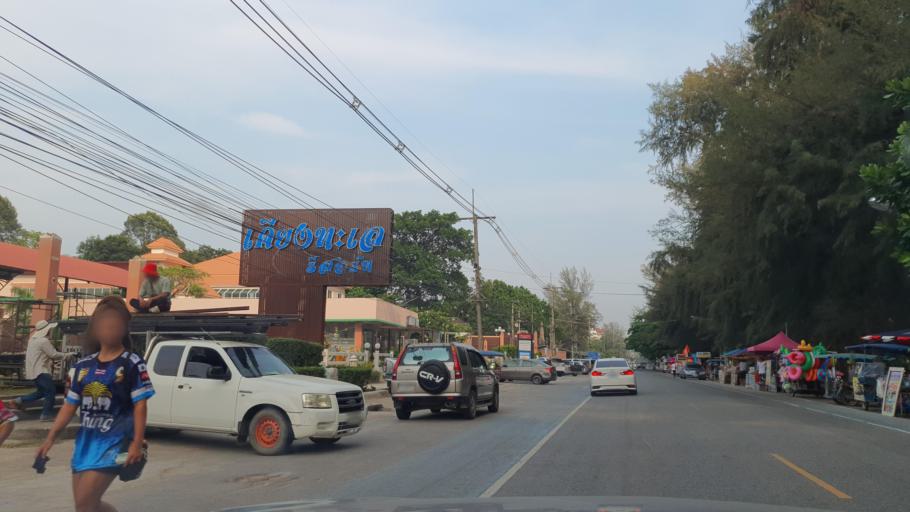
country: TH
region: Rayong
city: Rayong
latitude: 12.5984
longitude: 101.4073
